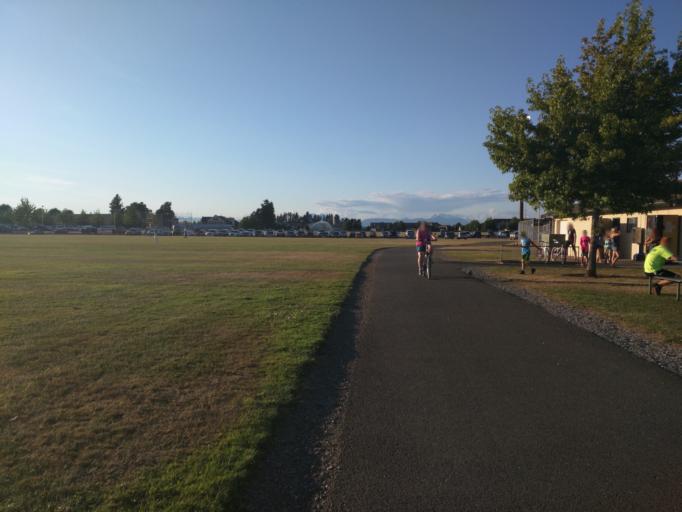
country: US
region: Washington
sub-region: Whatcom County
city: Lynden
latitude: 48.9584
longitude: -122.4382
